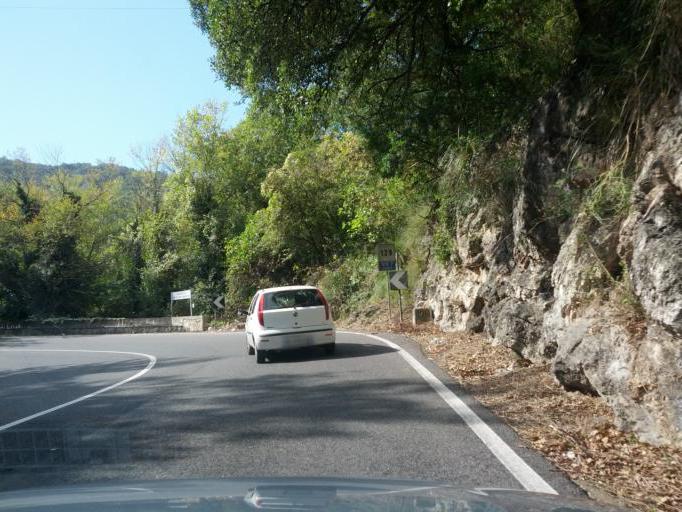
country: IT
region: Latium
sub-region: Provincia di Latina
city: Itri
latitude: 41.3040
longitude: 13.4950
